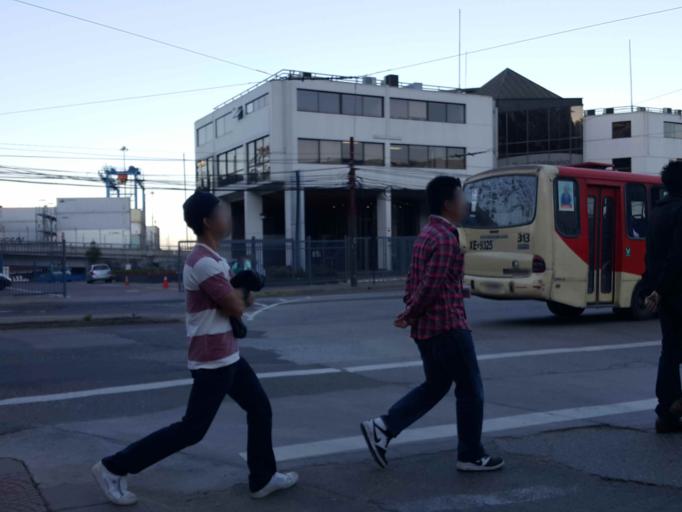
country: CL
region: Valparaiso
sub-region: Provincia de Valparaiso
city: Valparaiso
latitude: -33.0339
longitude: -71.6301
